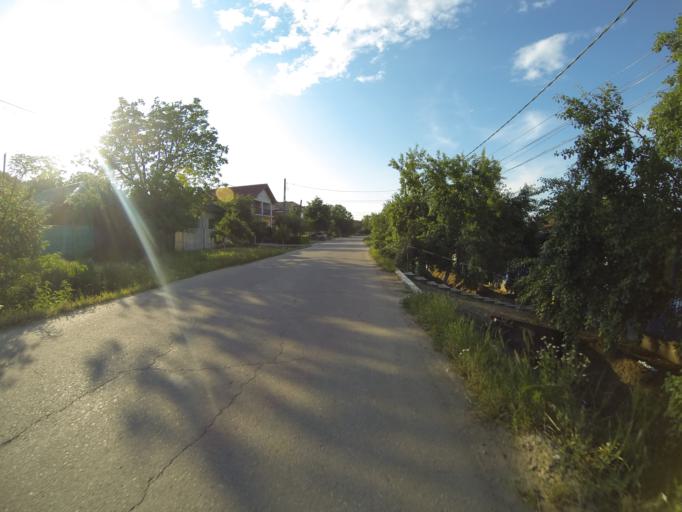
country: RO
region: Dolj
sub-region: Comuna Tuglui
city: Tuglui
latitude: 44.2096
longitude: 23.7945
